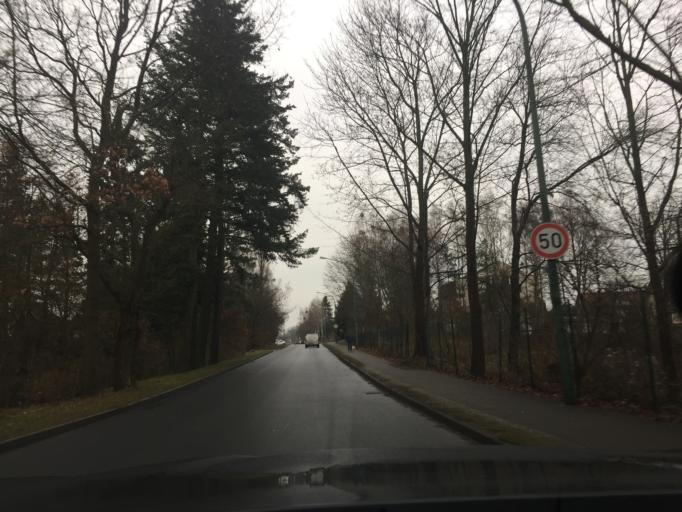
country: DE
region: Berlin
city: Kladow
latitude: 52.4671
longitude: 13.1016
